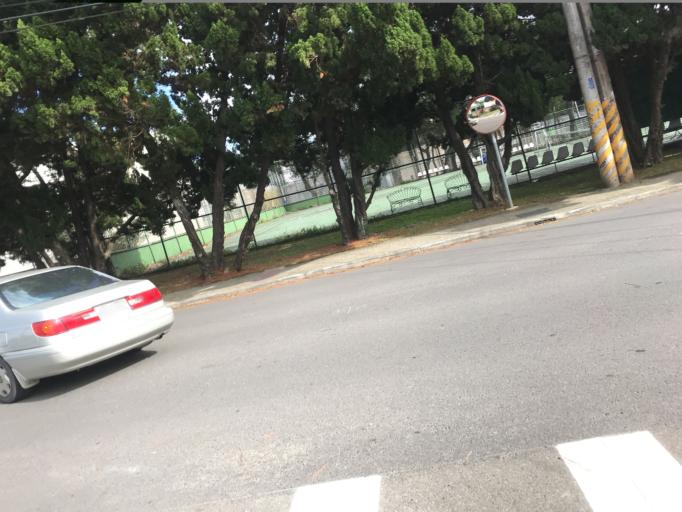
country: TW
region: Taiwan
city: Daxi
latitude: 24.8371
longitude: 121.2405
